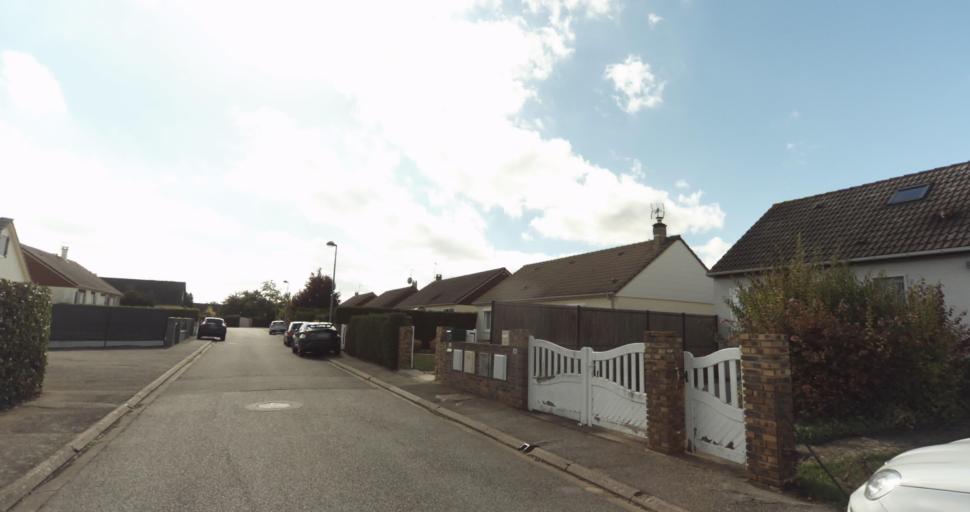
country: FR
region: Centre
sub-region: Departement d'Eure-et-Loir
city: Garnay
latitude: 48.7284
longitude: 1.3251
